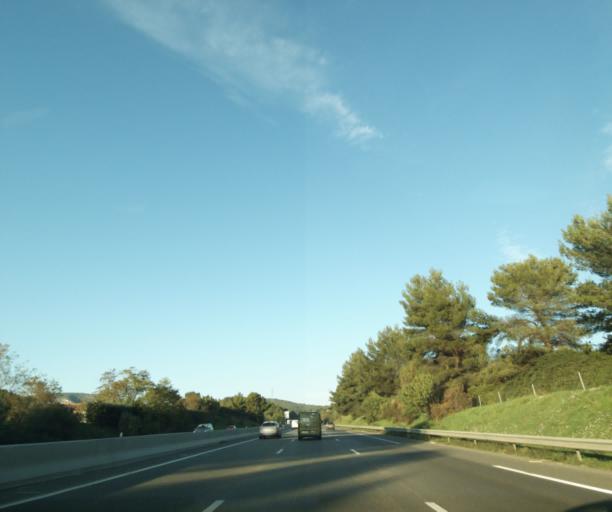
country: FR
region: Provence-Alpes-Cote d'Azur
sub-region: Departement des Bouches-du-Rhone
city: Roquevaire
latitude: 43.3352
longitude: 5.6063
